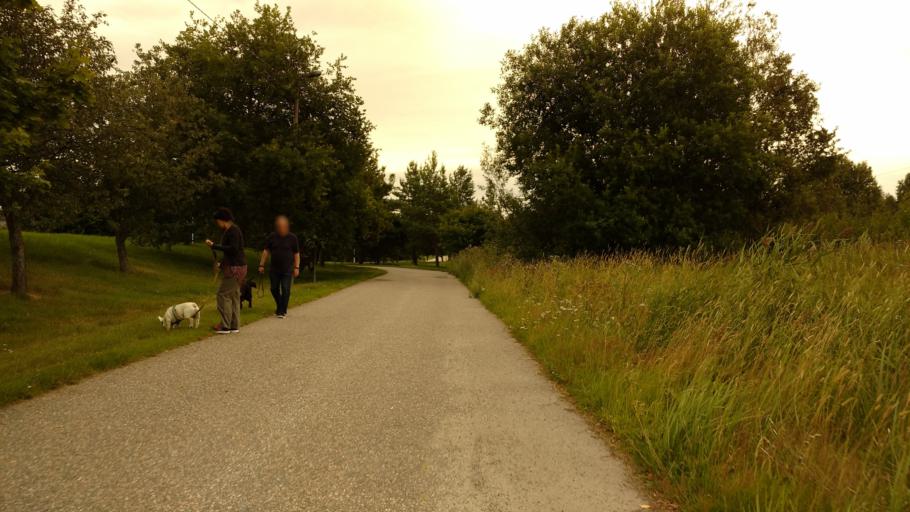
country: FI
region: Varsinais-Suomi
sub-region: Turku
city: Kaarina
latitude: 60.4378
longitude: 22.3364
